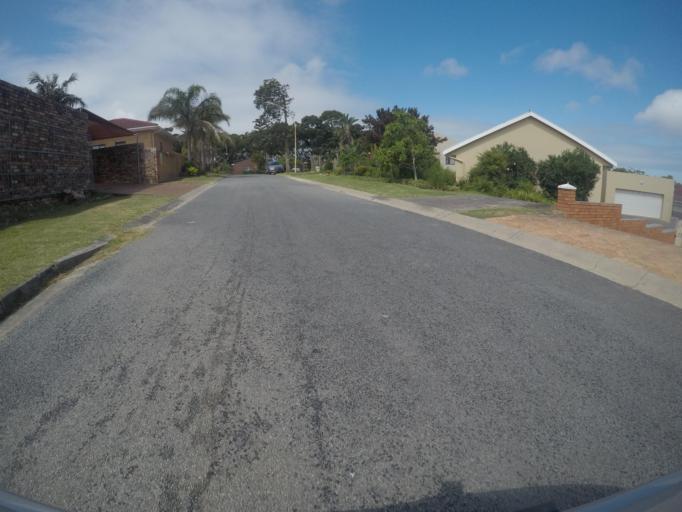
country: ZA
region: Eastern Cape
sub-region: Buffalo City Metropolitan Municipality
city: East London
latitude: -32.9981
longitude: 27.8879
